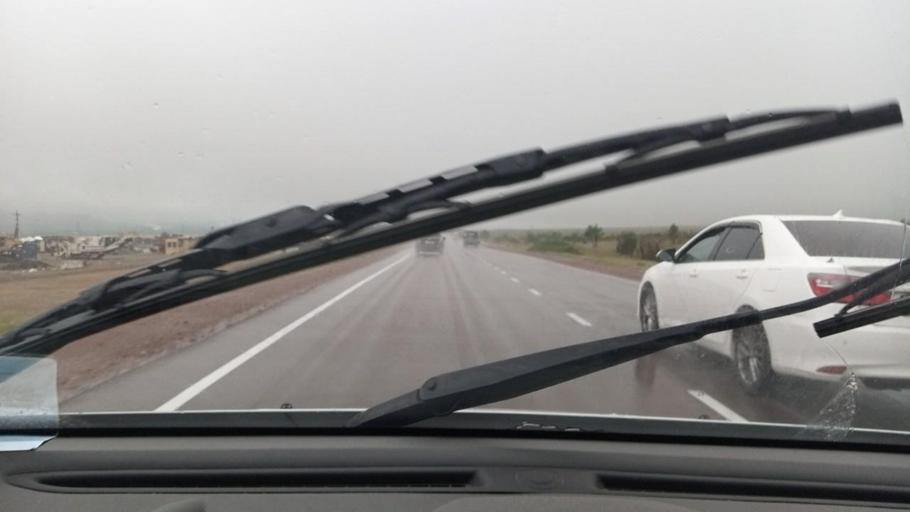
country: UZ
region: Toshkent
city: Angren
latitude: 41.0472
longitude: 70.1550
